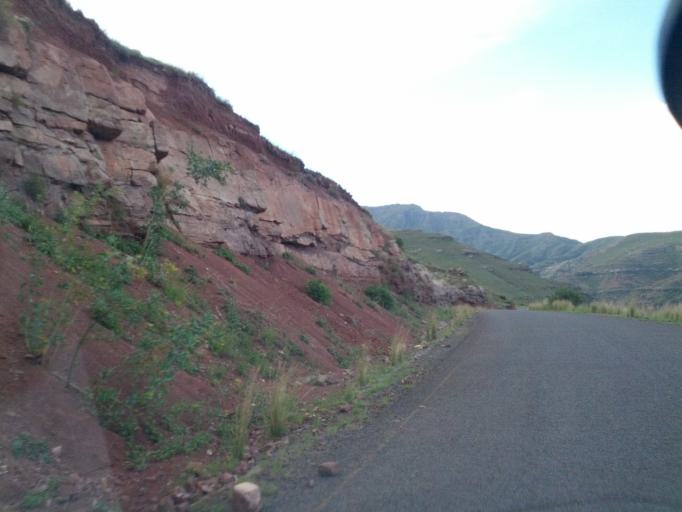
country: LS
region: Qacha's Nek
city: Qacha's Nek
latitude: -30.0579
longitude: 28.5030
